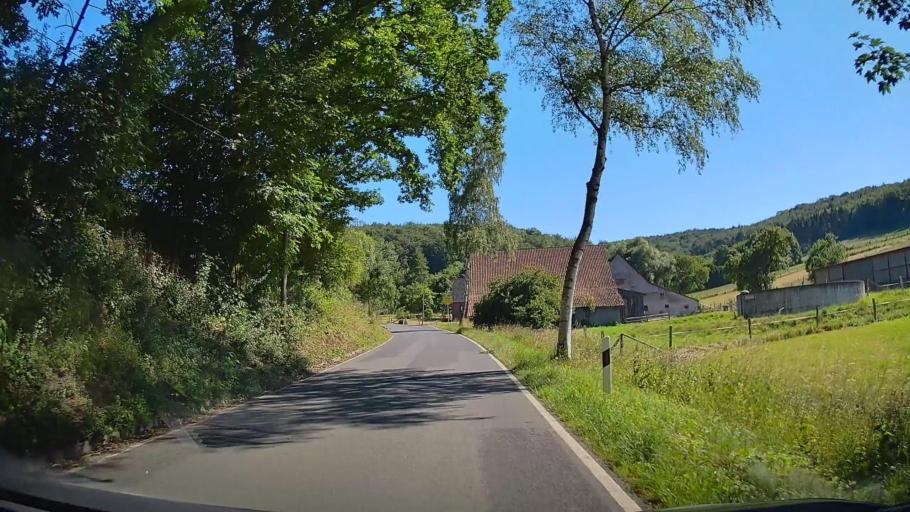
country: DE
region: Lower Saxony
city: Vahlbruch
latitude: 51.9796
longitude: 9.3487
